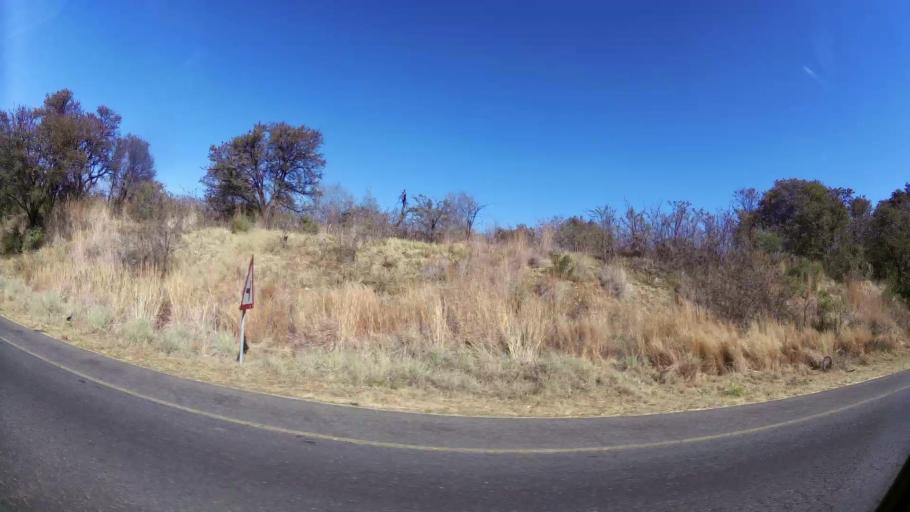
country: ZA
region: Gauteng
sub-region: City of Johannesburg Metropolitan Municipality
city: Johannesburg
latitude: -26.2888
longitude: 28.0390
